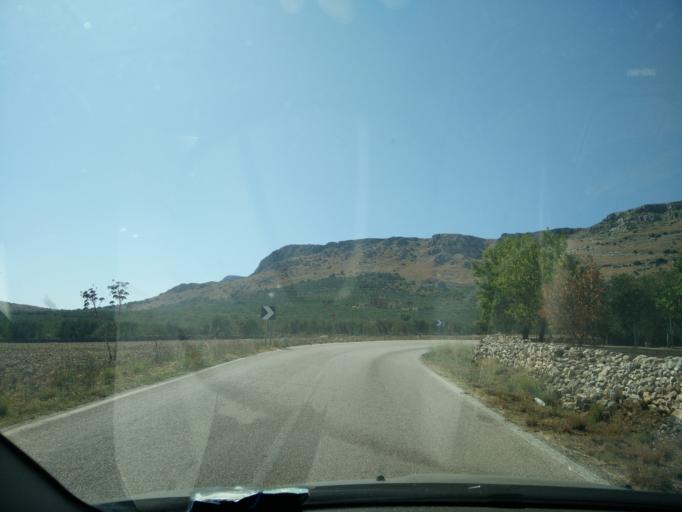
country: IT
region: Apulia
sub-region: Provincia di Foggia
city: Manfredonia
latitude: 41.6563
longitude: 15.8853
